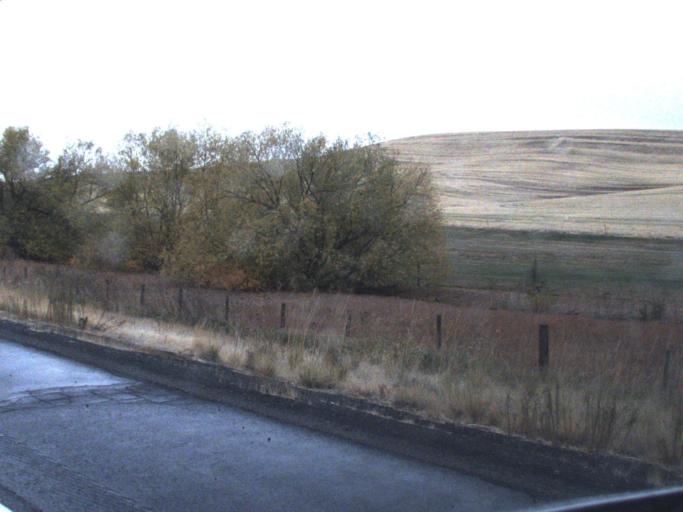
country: US
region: Washington
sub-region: Whitman County
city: Pullman
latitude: 46.7317
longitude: -117.2240
